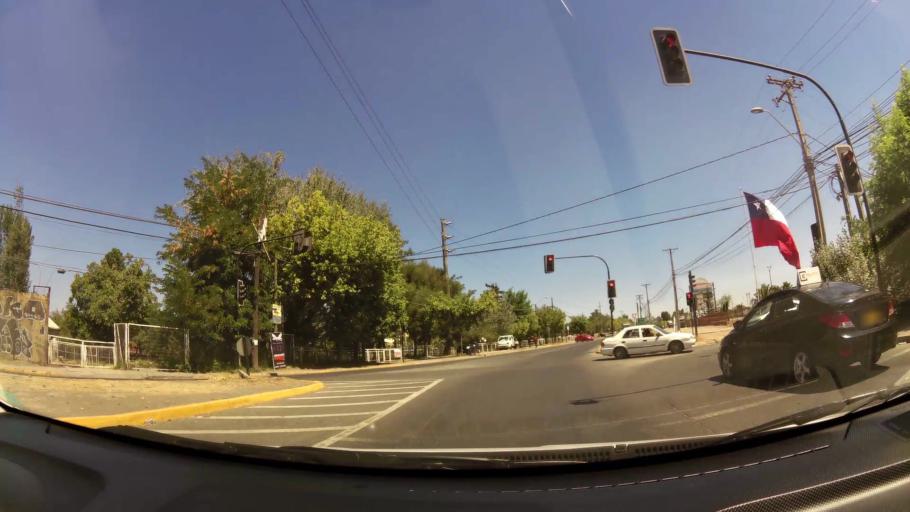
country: CL
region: O'Higgins
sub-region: Provincia de Cachapoal
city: Rancagua
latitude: -34.1660
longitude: -70.7722
